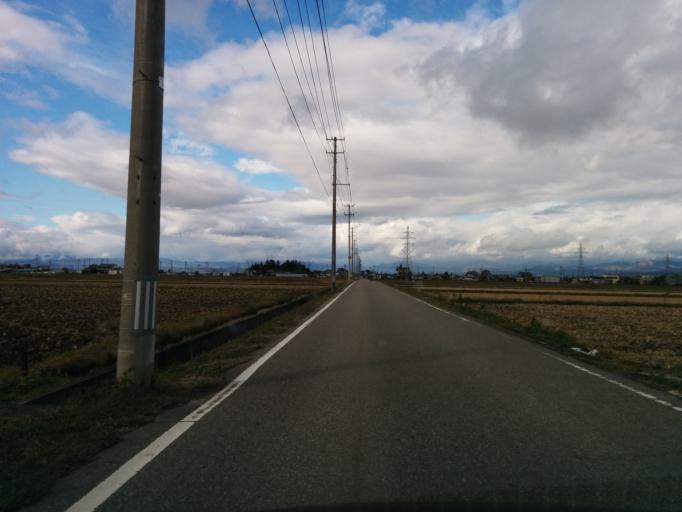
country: JP
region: Fukushima
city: Kitakata
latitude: 37.4992
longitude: 139.9073
